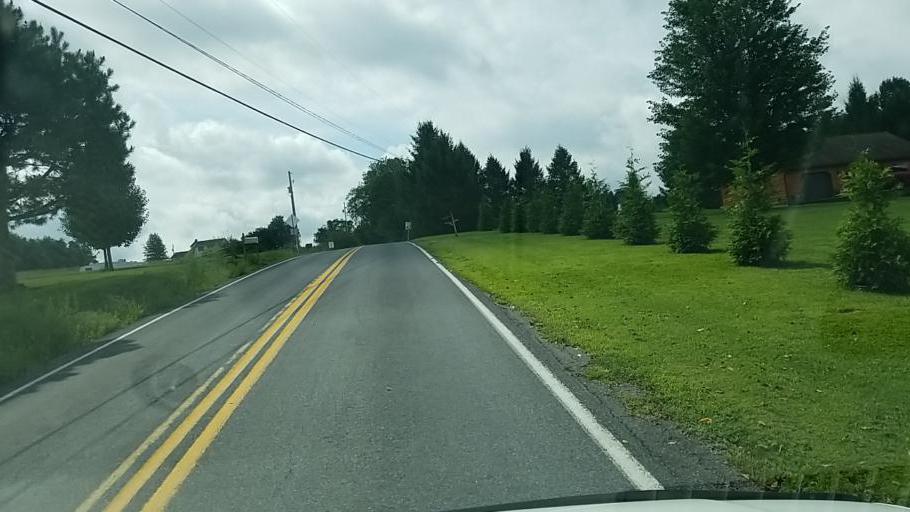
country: US
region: Pennsylvania
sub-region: Dauphin County
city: Millersburg
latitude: 40.5660
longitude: -76.8956
